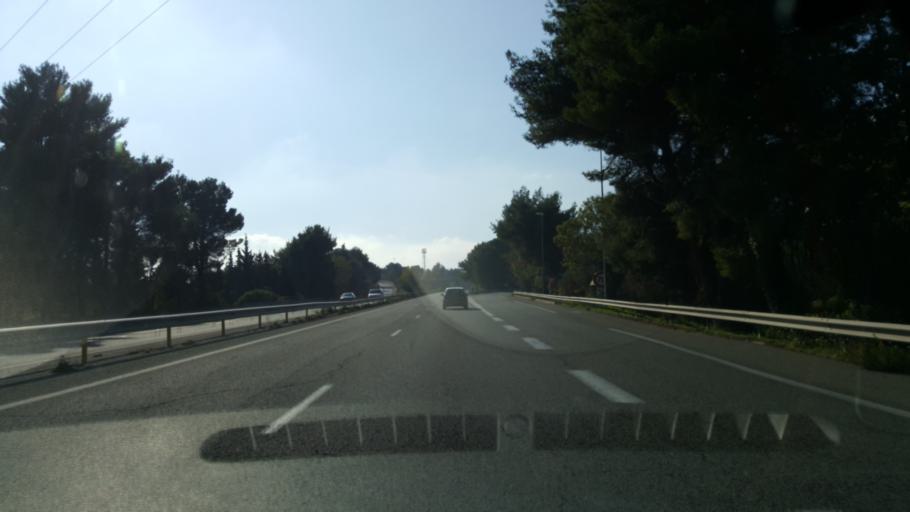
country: FR
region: Provence-Alpes-Cote d'Azur
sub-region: Departement des Bouches-du-Rhone
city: Aubagne
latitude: 43.3071
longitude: 5.5763
